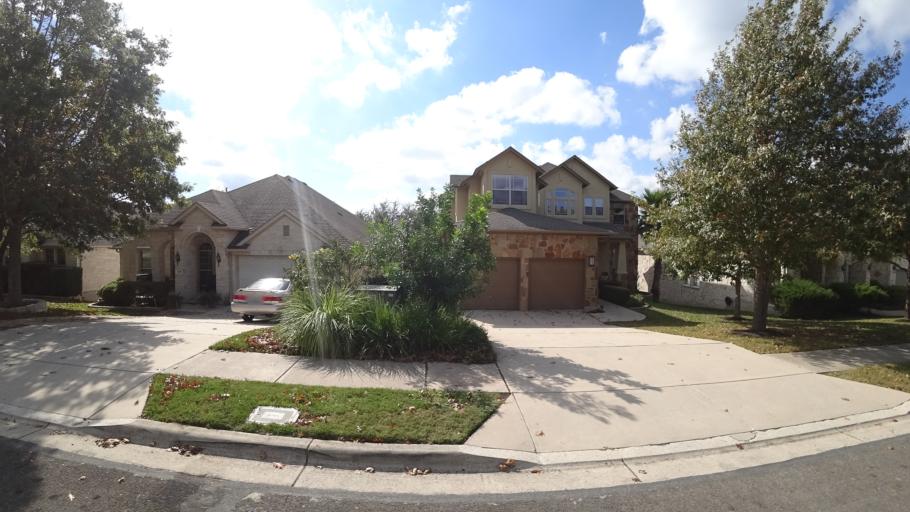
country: US
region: Texas
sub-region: Travis County
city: Barton Creek
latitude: 30.2545
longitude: -97.8863
